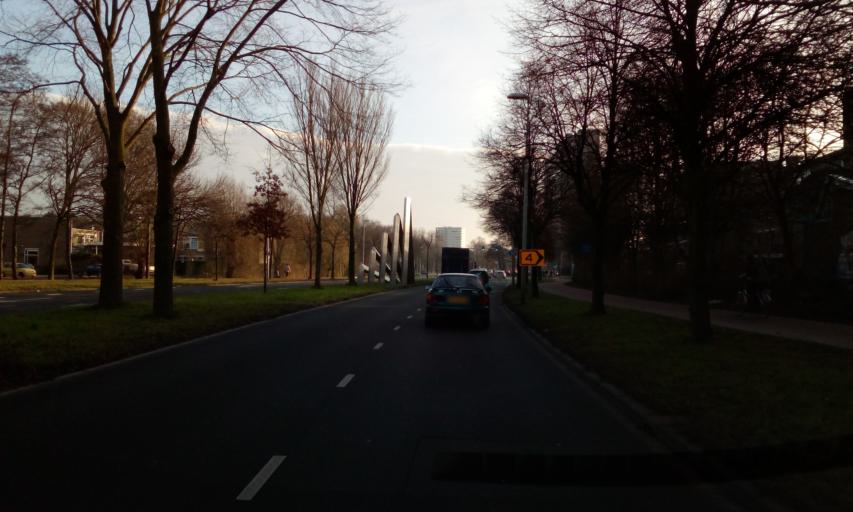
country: NL
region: South Holland
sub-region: Gemeente Westland
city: Kwintsheul
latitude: 52.0551
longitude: 4.2547
